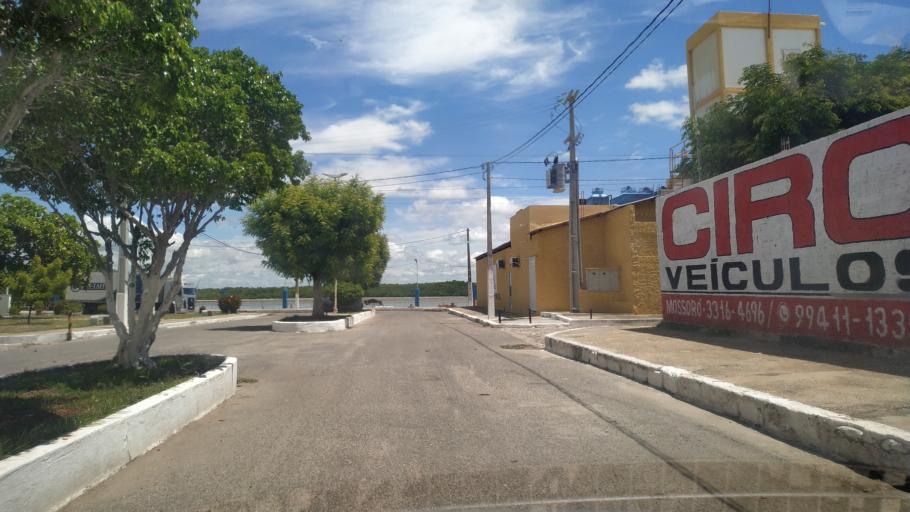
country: BR
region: Rio Grande do Norte
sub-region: Areia Branca
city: Areia Branca
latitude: -4.9580
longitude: -37.1370
